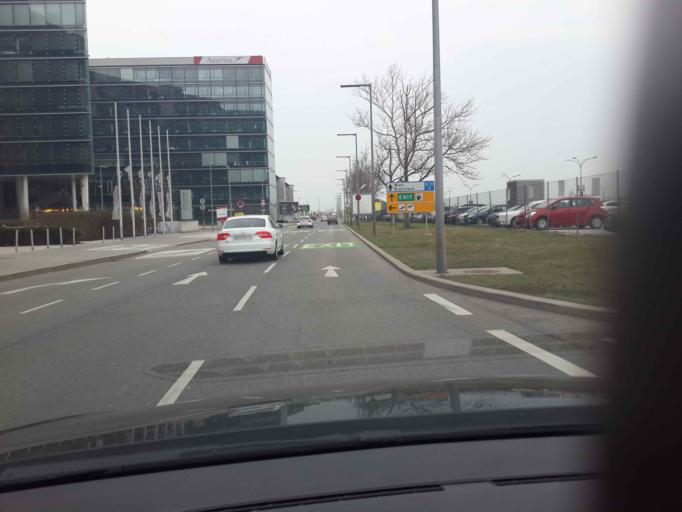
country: AT
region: Lower Austria
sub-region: Politischer Bezirk Wien-Umgebung
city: Fischamend Dorf
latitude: 48.1228
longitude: 16.5656
